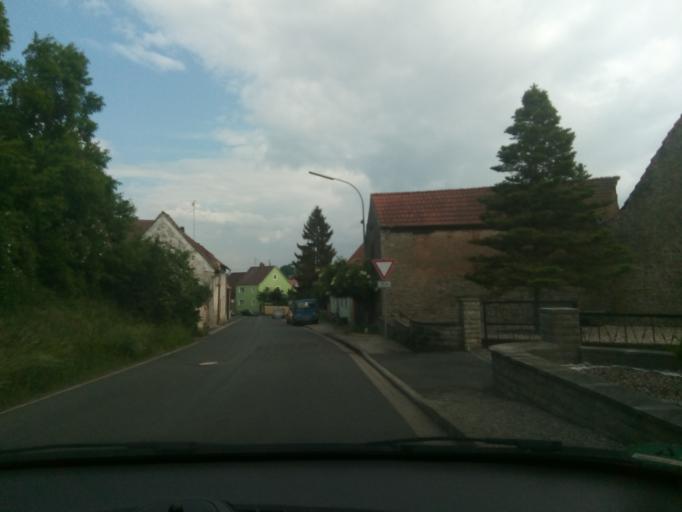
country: DE
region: Bavaria
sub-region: Regierungsbezirk Unterfranken
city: Frankenwinheim
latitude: 49.8851
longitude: 10.2836
